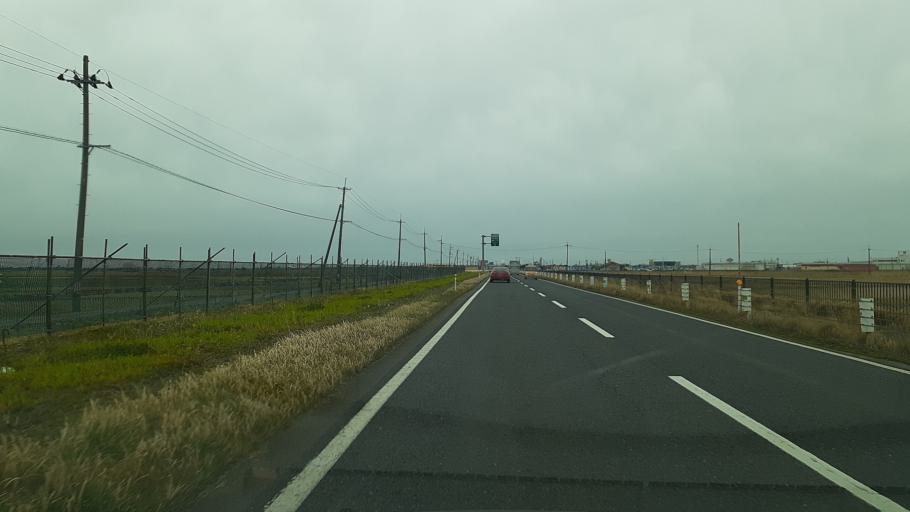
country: JP
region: Niigata
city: Niitsu-honcho
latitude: 37.8084
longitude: 139.1013
